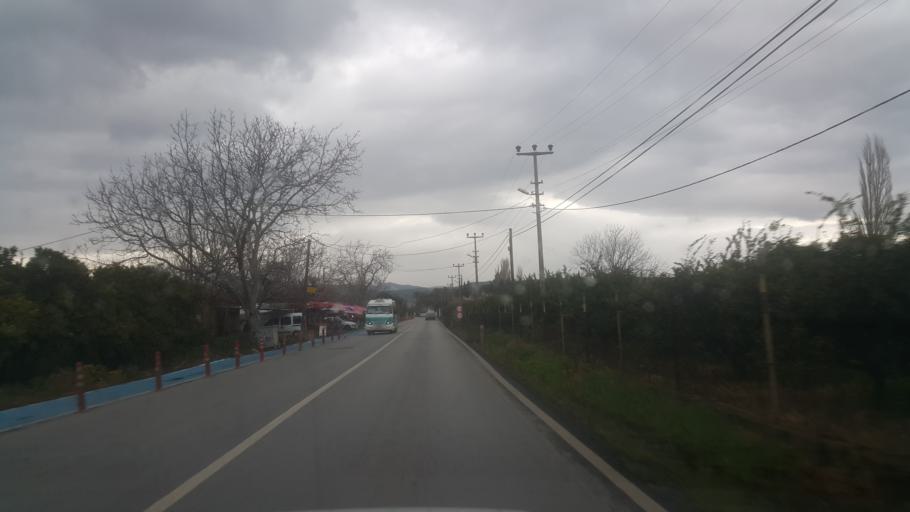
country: TR
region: Izmir
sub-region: Seferihisar
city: Seferhisar
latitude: 38.1907
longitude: 26.8176
